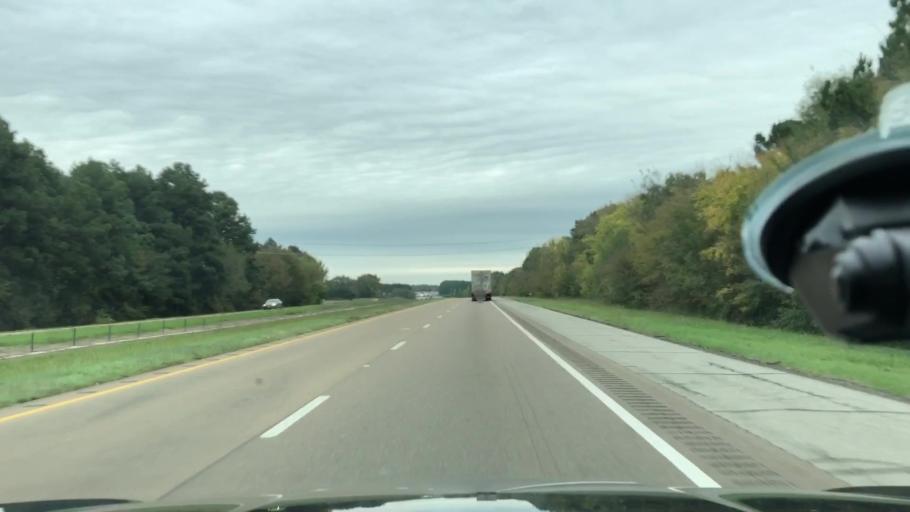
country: US
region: Texas
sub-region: Titus County
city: Mount Pleasant
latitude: 33.2141
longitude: -94.8991
